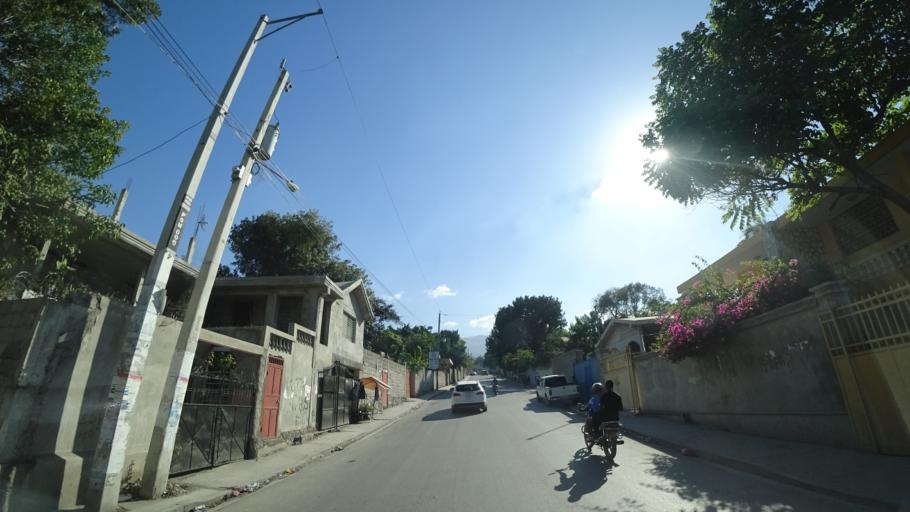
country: HT
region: Ouest
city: Petionville
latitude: 18.5245
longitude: -72.2826
